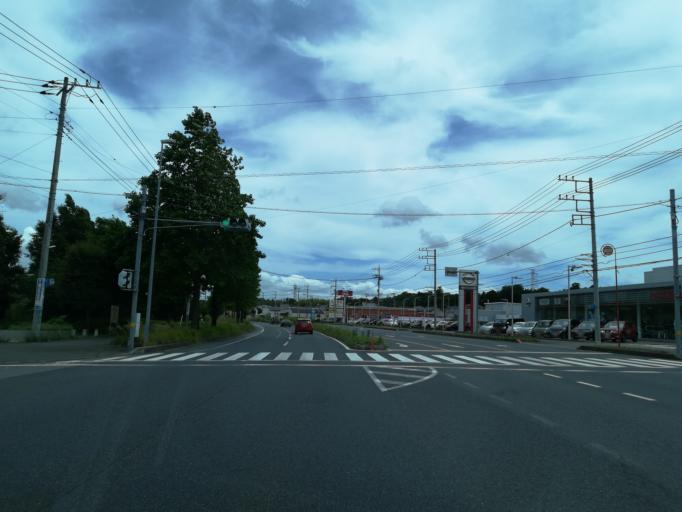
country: JP
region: Ibaraki
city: Naka
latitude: 36.0105
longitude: 140.1475
